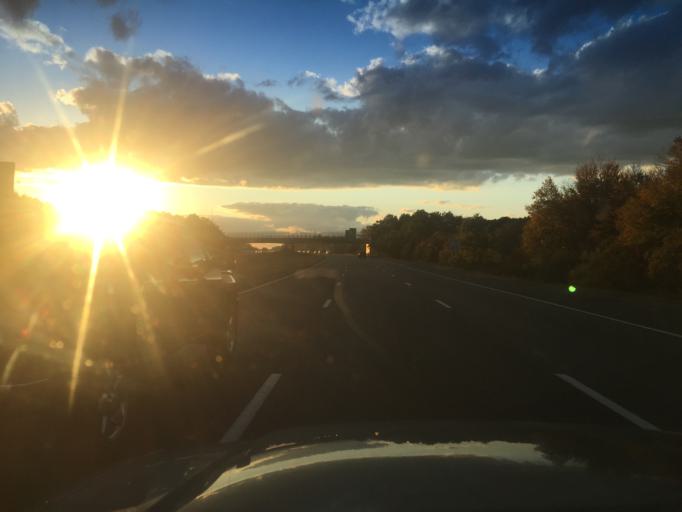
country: US
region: Massachusetts
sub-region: Bristol County
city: Raynham
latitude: 41.9571
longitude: -71.0407
